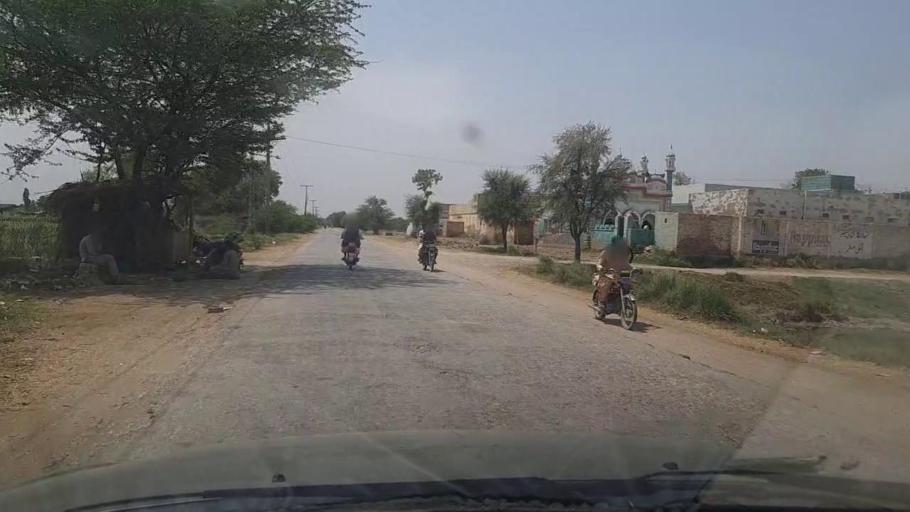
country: PK
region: Sindh
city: Bhiria
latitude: 26.8976
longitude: 68.2261
